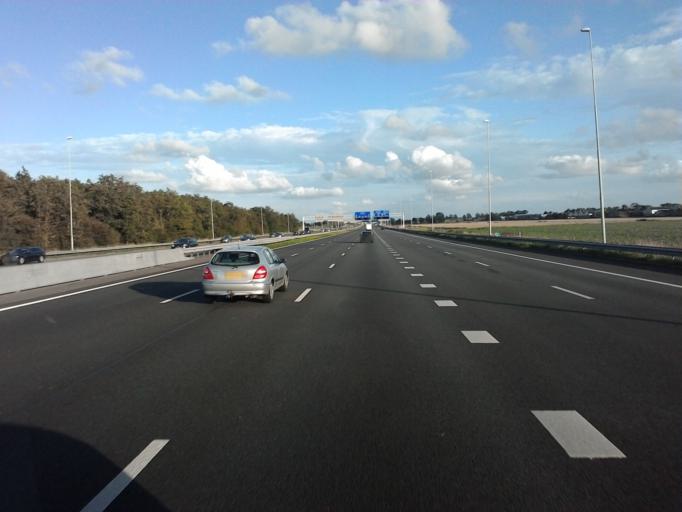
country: NL
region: North Holland
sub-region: Gemeente Haarlemmermeer
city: Hoofddorp
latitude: 52.3665
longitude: 4.7210
